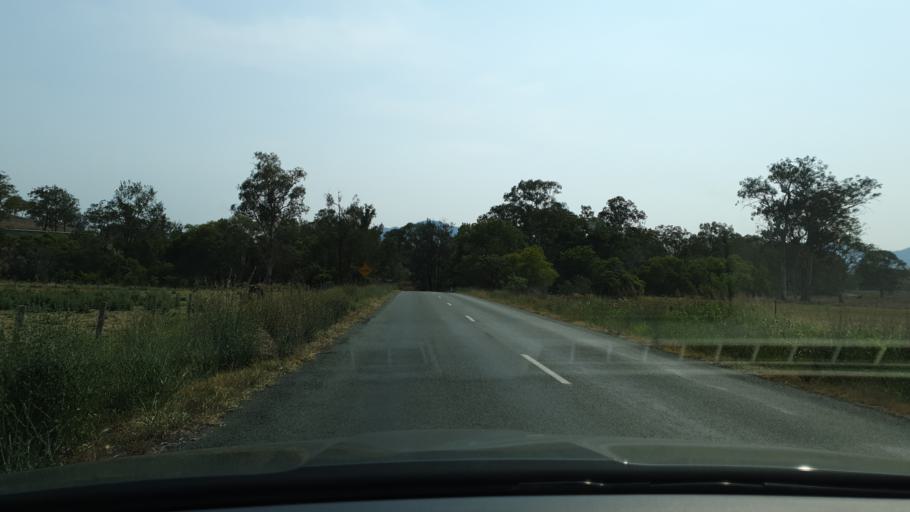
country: AU
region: Queensland
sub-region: Ipswich
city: Deebing Heights
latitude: -28.1441
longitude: 152.5672
